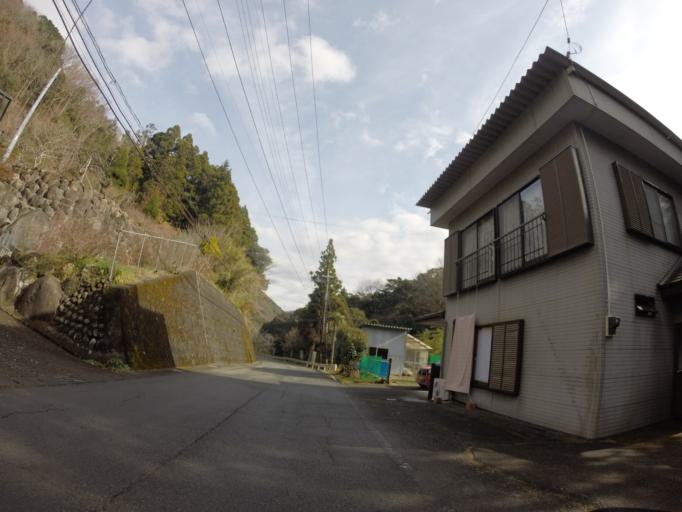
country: JP
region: Shizuoka
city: Heda
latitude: 34.8840
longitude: 138.9113
